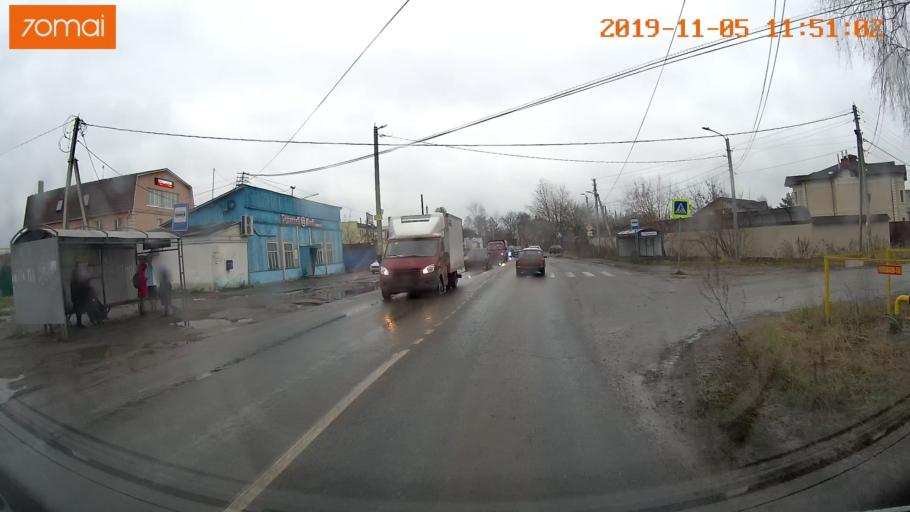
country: RU
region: Ivanovo
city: Bogorodskoye
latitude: 57.0070
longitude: 41.0246
